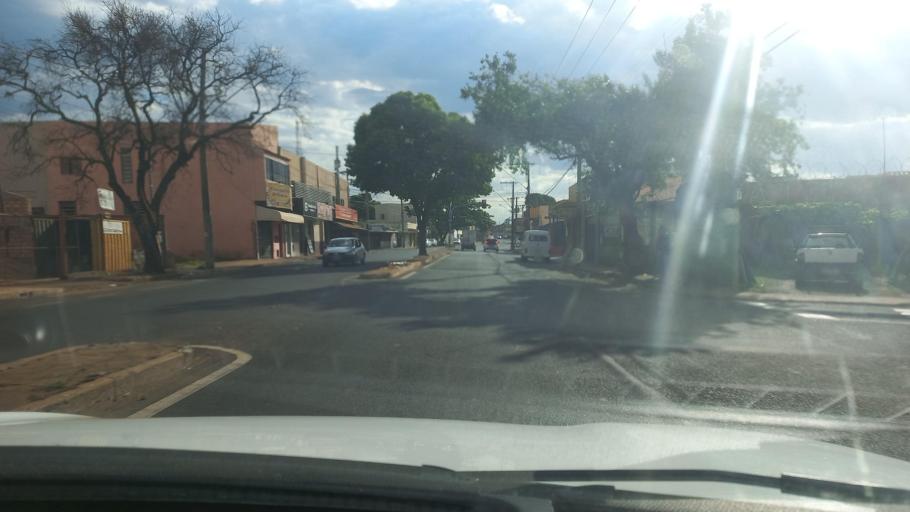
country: BR
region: Minas Gerais
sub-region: Uberaba
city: Uberaba
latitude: -19.7614
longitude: -47.9137
